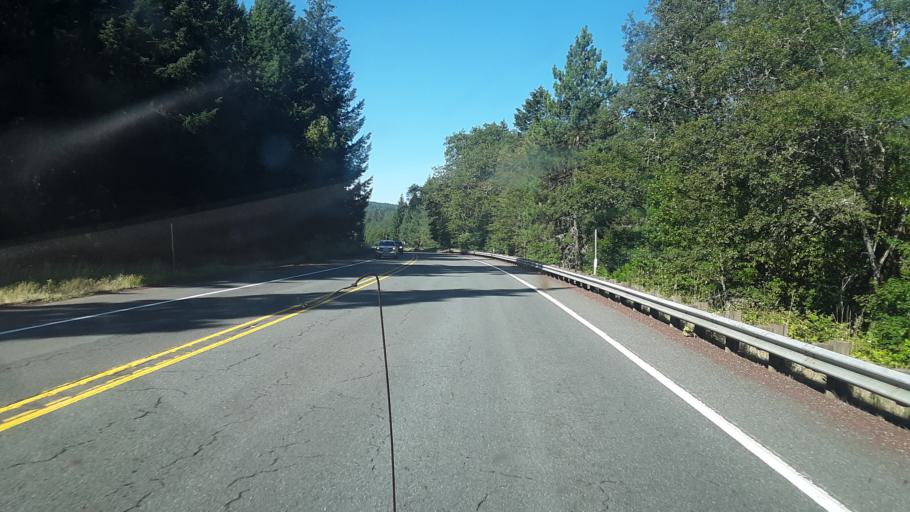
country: US
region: Oregon
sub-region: Jackson County
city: Shady Cove
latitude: 42.6864
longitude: -122.6089
